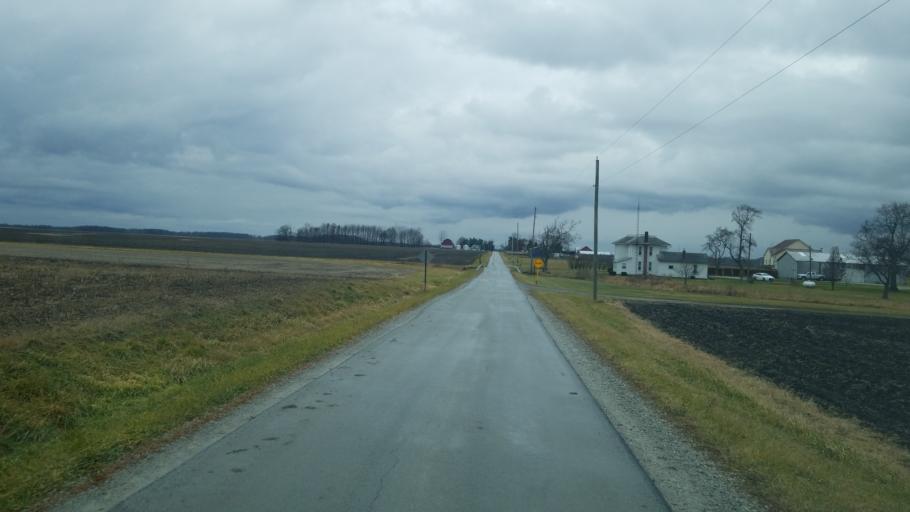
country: US
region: Ohio
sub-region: Wyandot County
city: Upper Sandusky
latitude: 40.7595
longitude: -83.3425
